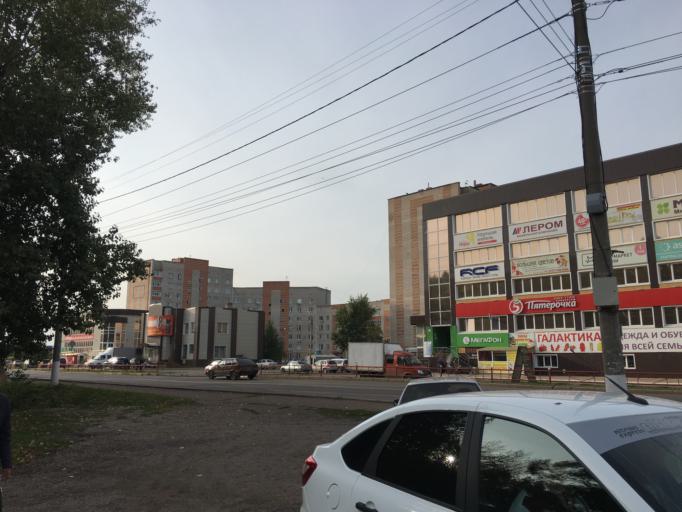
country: RU
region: Bashkortostan
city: Meleuz
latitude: 52.9598
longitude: 55.9232
